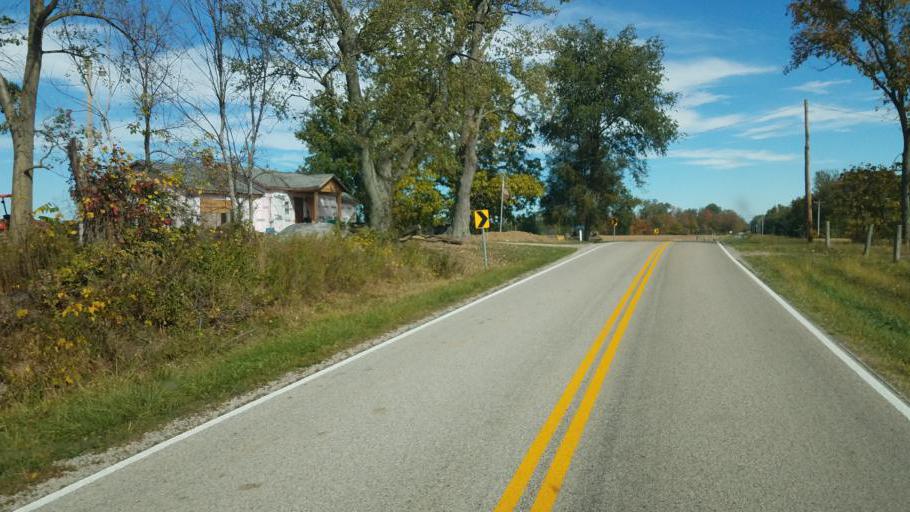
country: US
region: Ohio
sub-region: Huron County
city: New London
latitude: 41.1383
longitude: -82.4741
